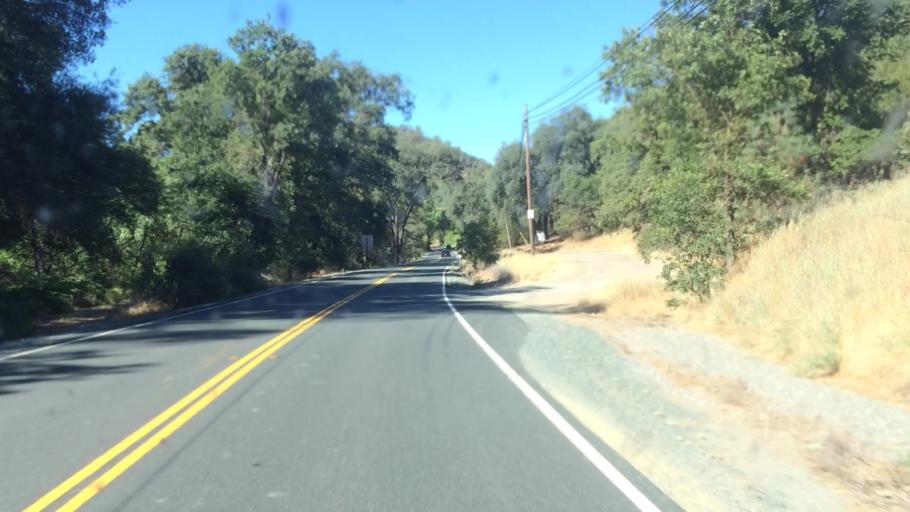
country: US
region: California
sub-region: Amador County
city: Plymouth
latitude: 38.5553
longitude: -120.8475
